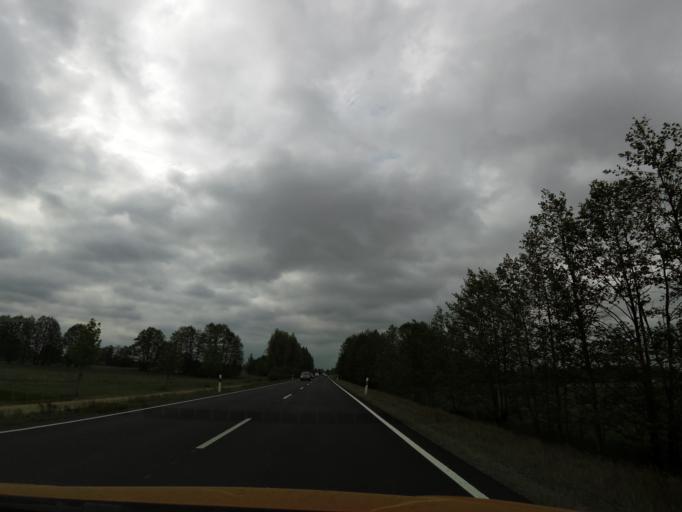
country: DE
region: Brandenburg
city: Beelitz
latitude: 52.2410
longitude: 12.9867
